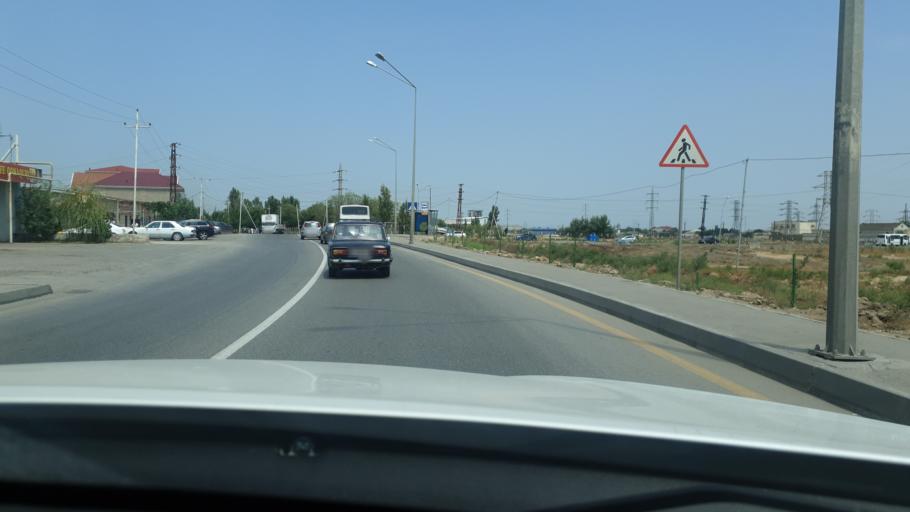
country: AZ
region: Baki
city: Qaracuxur
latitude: 40.3943
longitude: 49.9931
